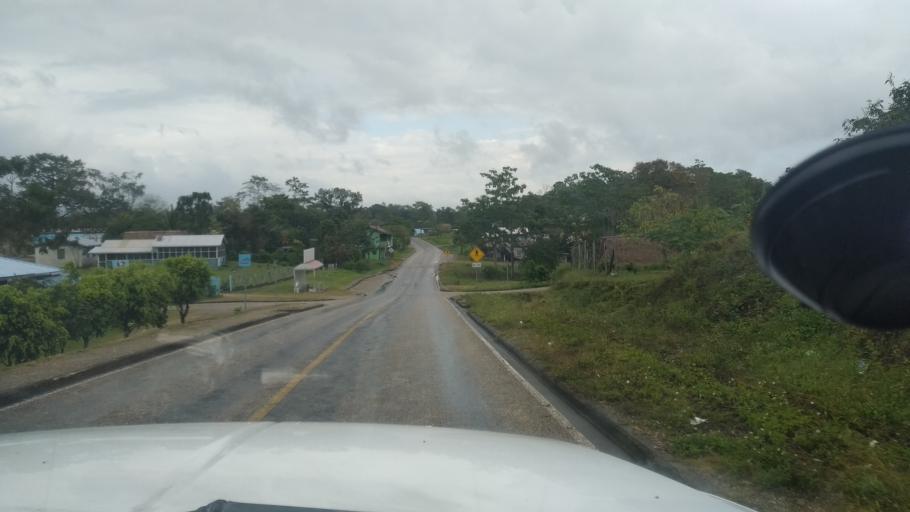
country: GT
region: Peten
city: San Luis
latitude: 16.2067
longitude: -89.1397
